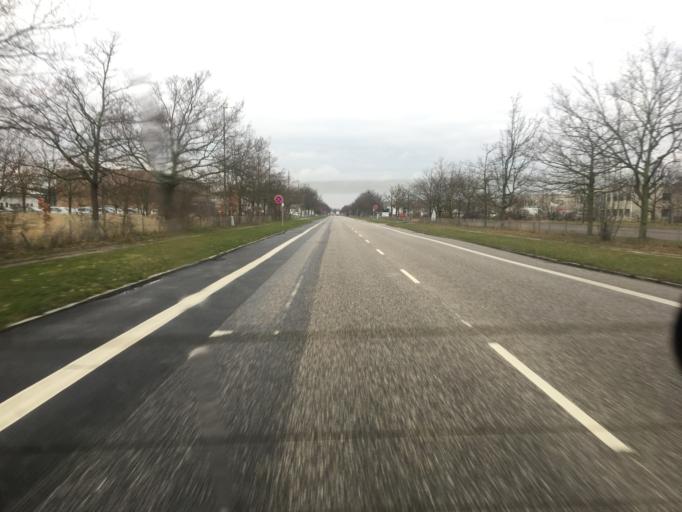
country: DK
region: Capital Region
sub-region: Hvidovre Kommune
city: Hvidovre
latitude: 55.6060
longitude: 12.4891
